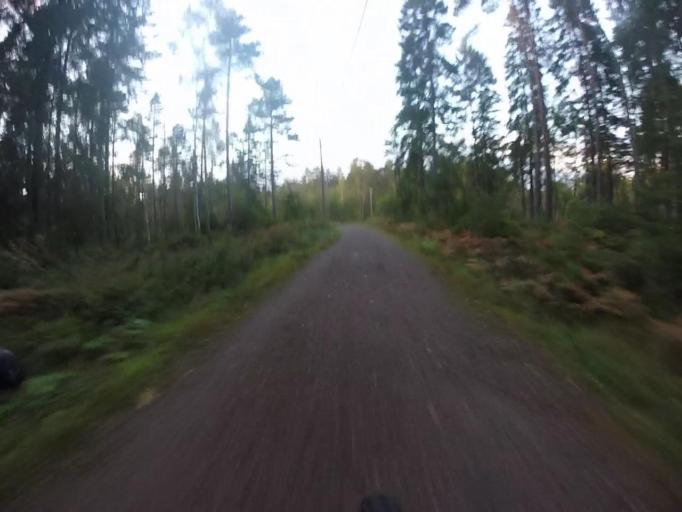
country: SE
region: Vaestra Goetaland
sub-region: Trollhattan
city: Trollhattan
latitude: 58.2991
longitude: 12.2664
